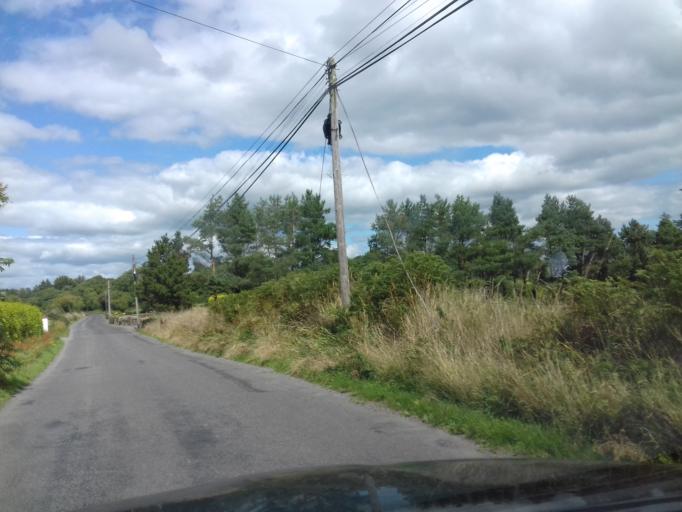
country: IE
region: Munster
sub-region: Waterford
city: Tra Mhor
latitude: 52.1742
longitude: -7.2368
